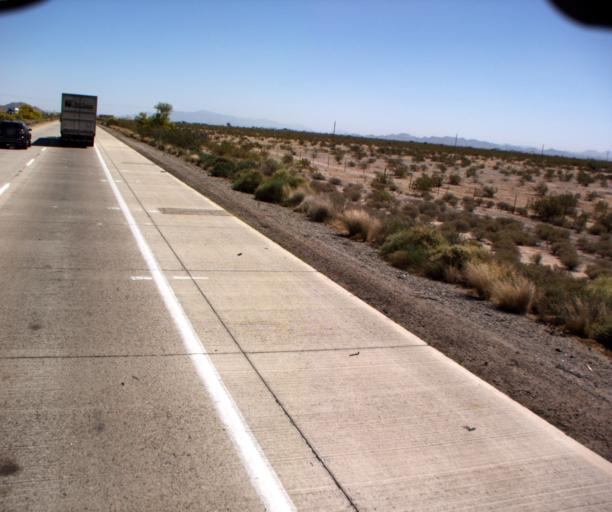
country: US
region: Arizona
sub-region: Maricopa County
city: Buckeye
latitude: 33.4436
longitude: -112.6976
